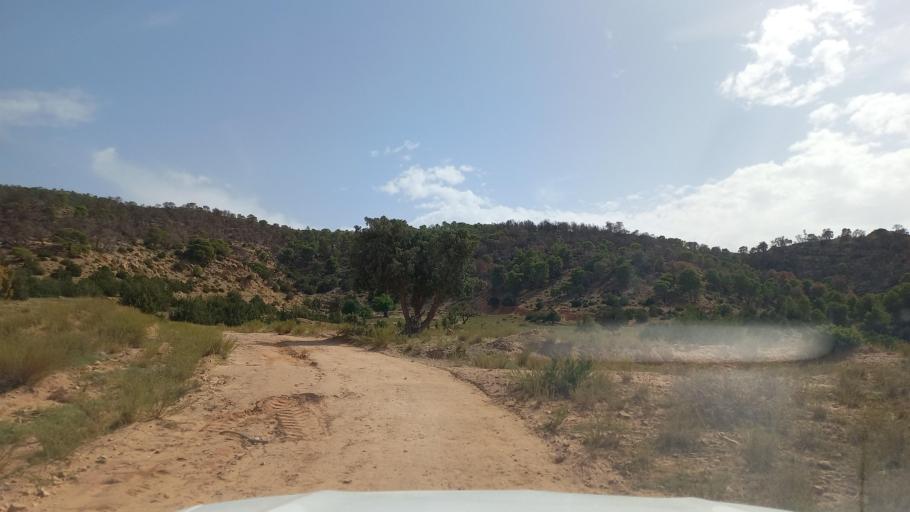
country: TN
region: Al Qasrayn
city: Kasserine
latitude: 35.3540
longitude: 8.8900
